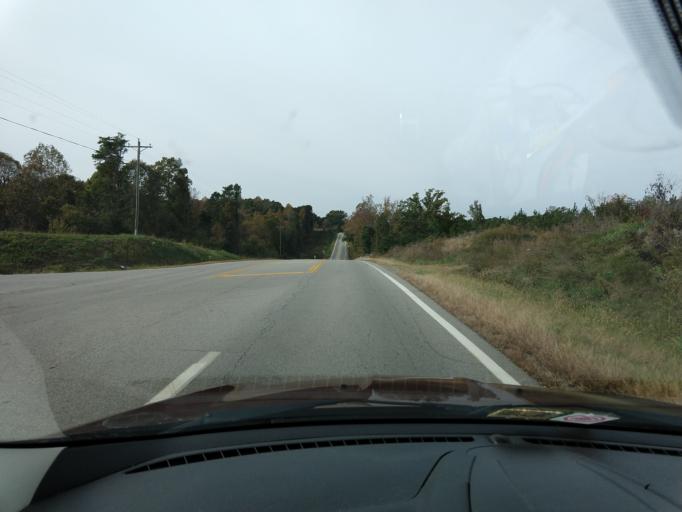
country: US
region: Virginia
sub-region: Pittsylvania County
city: Gretna
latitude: 36.9434
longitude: -79.4991
